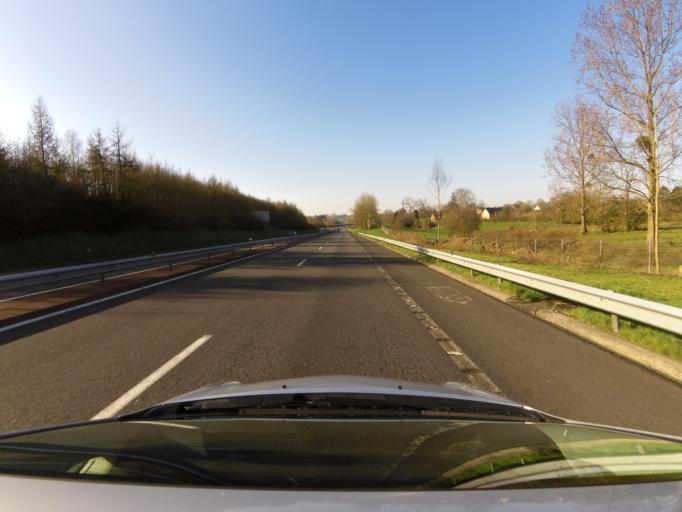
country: FR
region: Lower Normandy
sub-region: Departement de la Manche
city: Villedieu-les-Poeles
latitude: 48.8095
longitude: -1.2572
